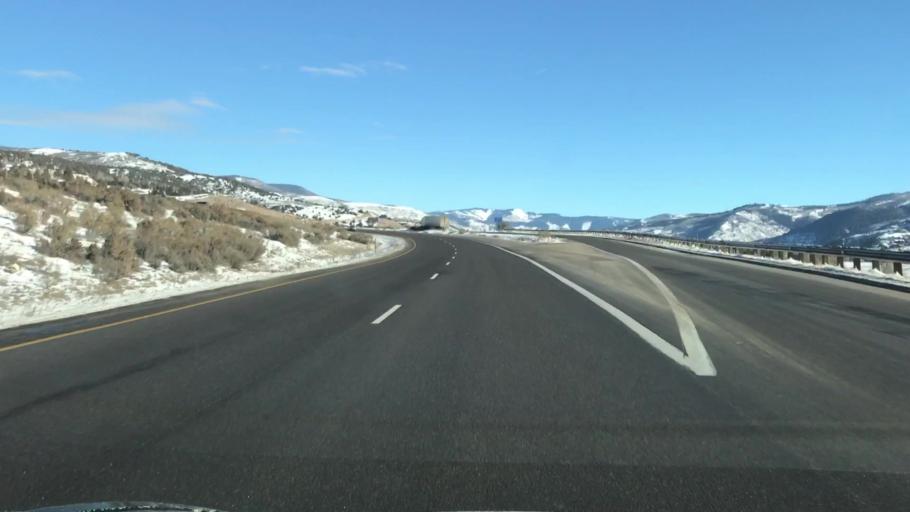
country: US
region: Colorado
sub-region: Eagle County
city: Edwards
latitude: 39.6529
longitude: -106.6116
